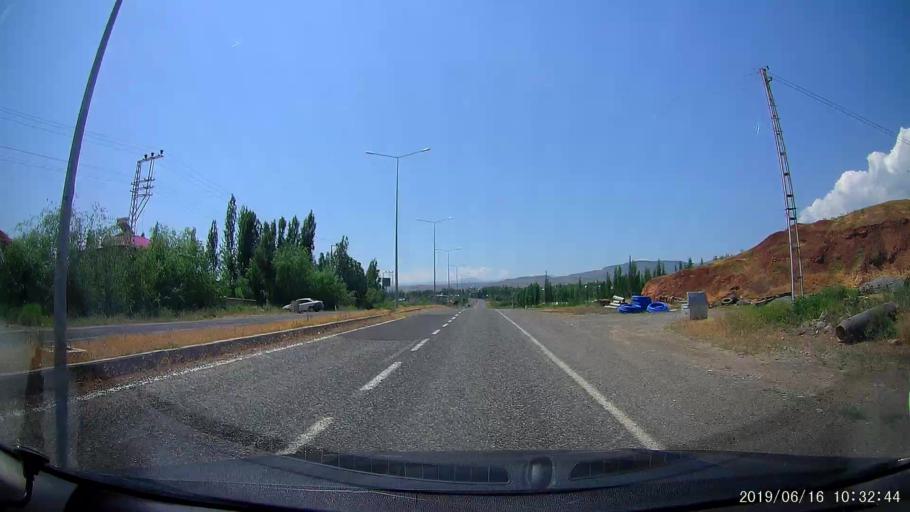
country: TR
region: Igdir
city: Tuzluca
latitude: 40.0475
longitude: 43.6540
